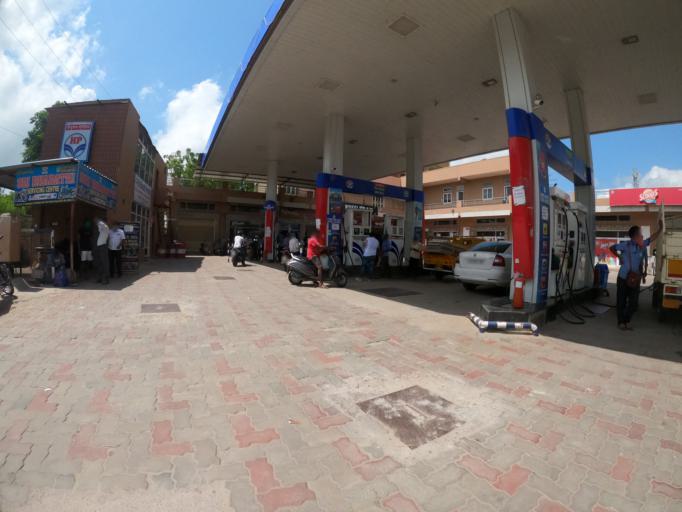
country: IN
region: Telangana
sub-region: Hyderabad
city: Hyderabad
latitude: 17.3592
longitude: 78.3878
